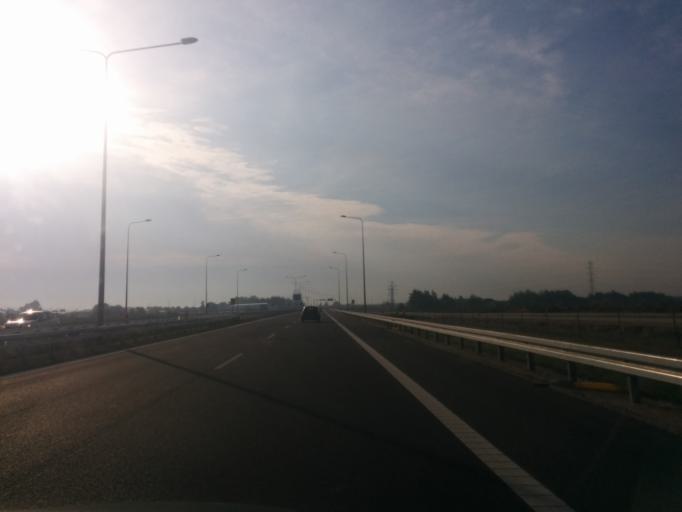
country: PL
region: Masovian Voivodeship
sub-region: Powiat pruszkowski
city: Nowe Grocholice
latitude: 52.1204
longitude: 20.8826
